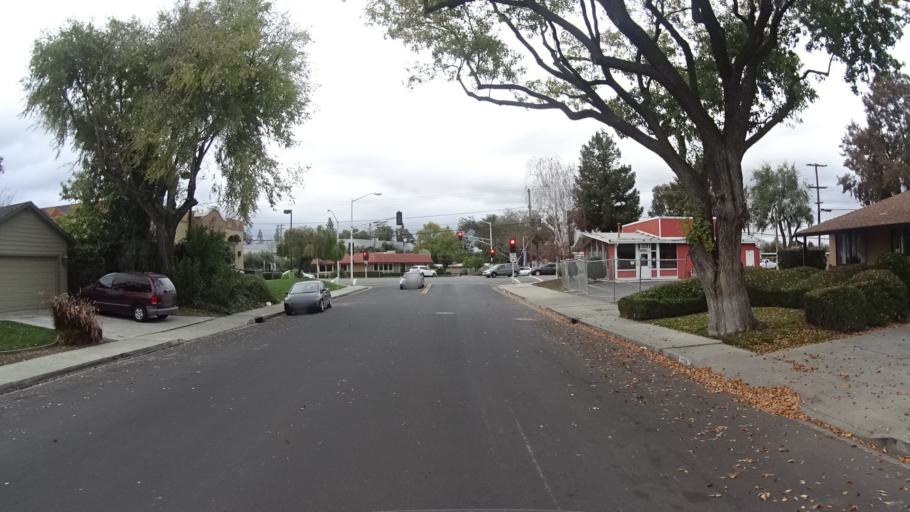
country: US
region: California
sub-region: Santa Clara County
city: Santa Clara
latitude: 37.3391
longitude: -121.9721
